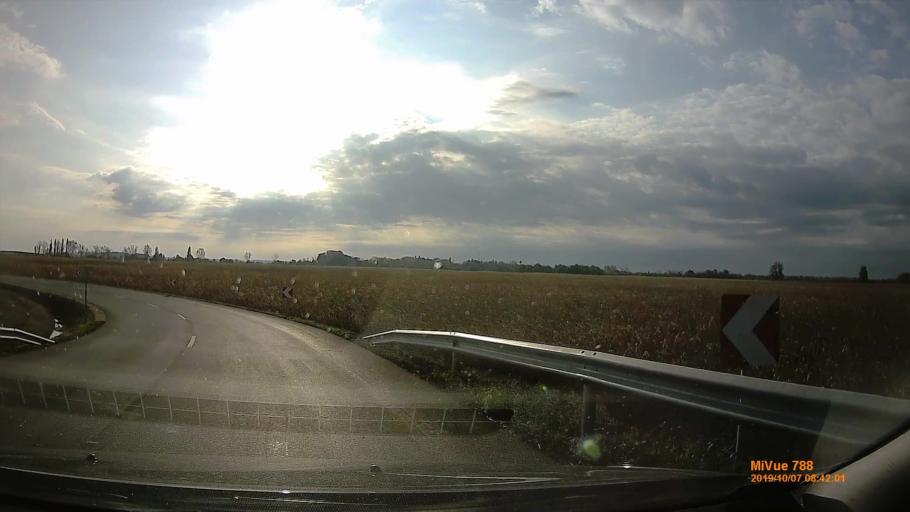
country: HU
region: Bekes
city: Szarvas
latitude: 46.8174
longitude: 20.5171
